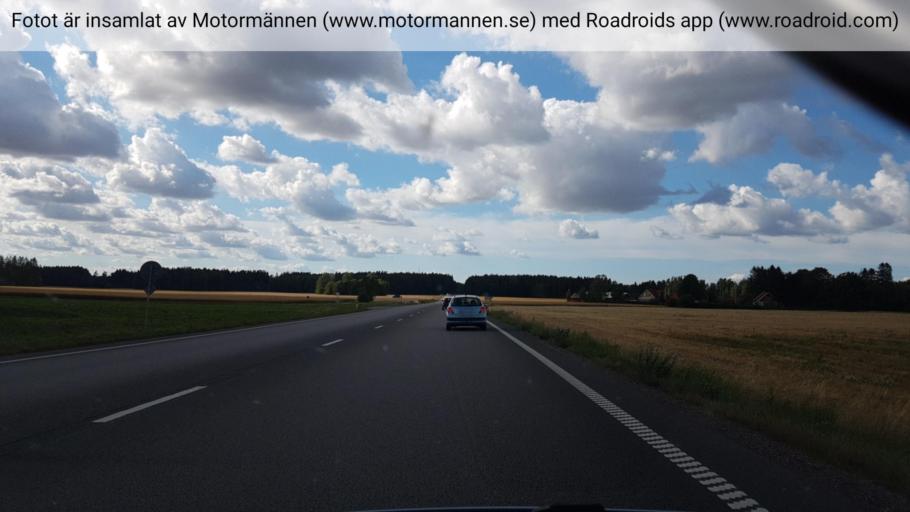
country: SE
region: Vaestra Goetaland
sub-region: Skara Kommun
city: Skara
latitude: 58.4094
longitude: 13.3827
